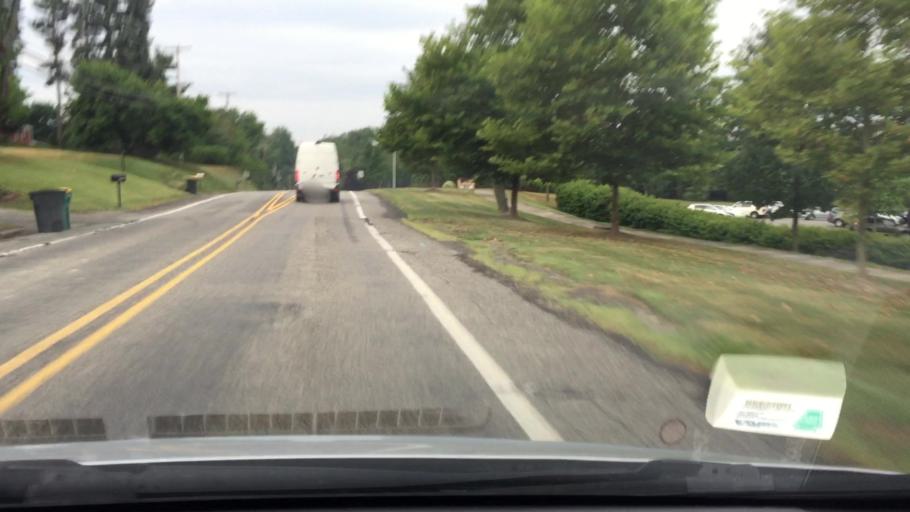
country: US
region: Pennsylvania
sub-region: Allegheny County
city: Franklin Park
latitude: 40.6098
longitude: -80.0998
